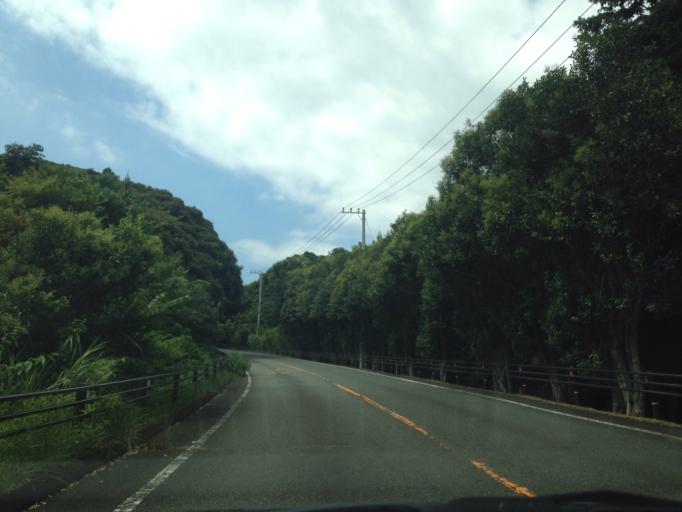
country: JP
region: Shizuoka
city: Shimoda
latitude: 34.6852
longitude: 138.7782
